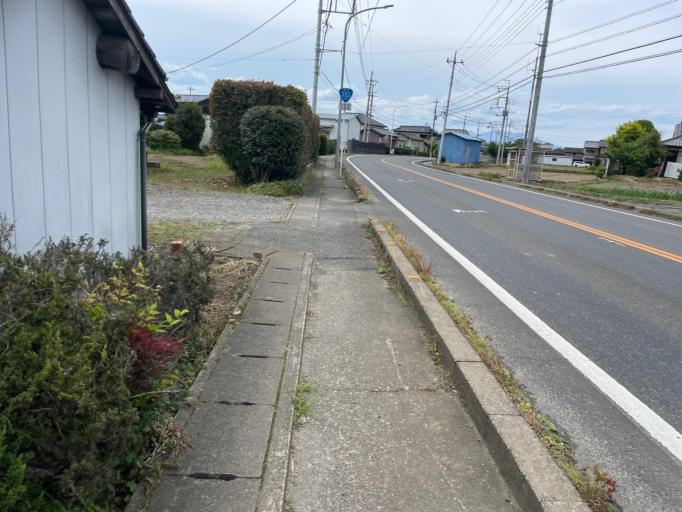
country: JP
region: Tochigi
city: Mibu
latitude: 36.4578
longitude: 139.7724
